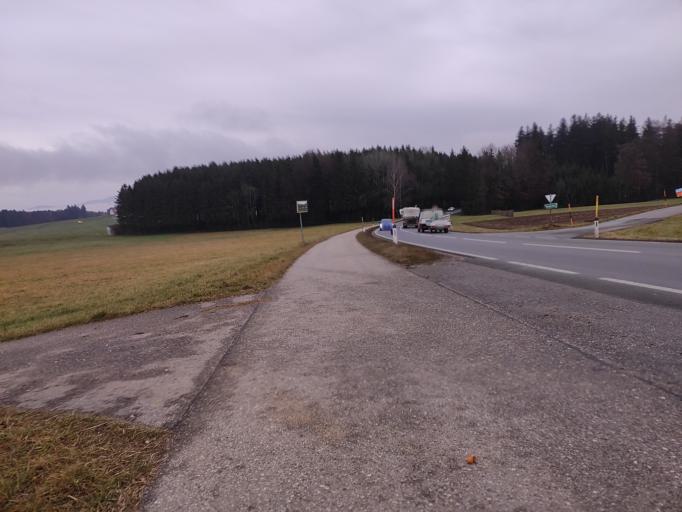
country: AT
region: Salzburg
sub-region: Politischer Bezirk Salzburg-Umgebung
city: Seekirchen am Wallersee
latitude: 47.9188
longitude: 13.1059
